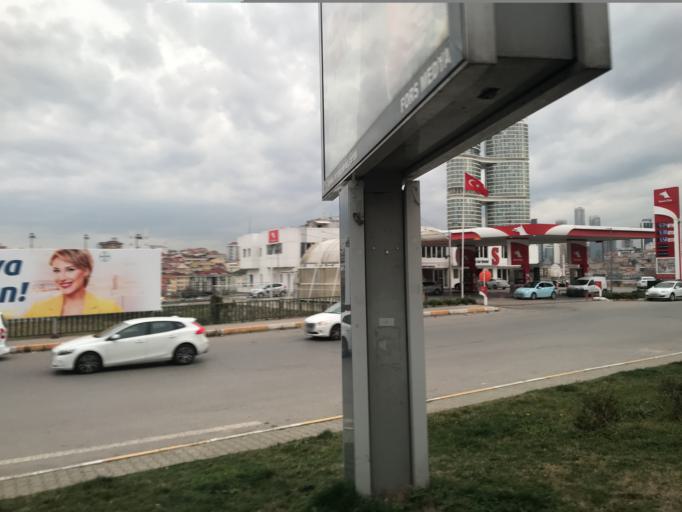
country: TR
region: Istanbul
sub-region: Atasehir
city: Atasehir
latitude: 40.9896
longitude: 29.0817
